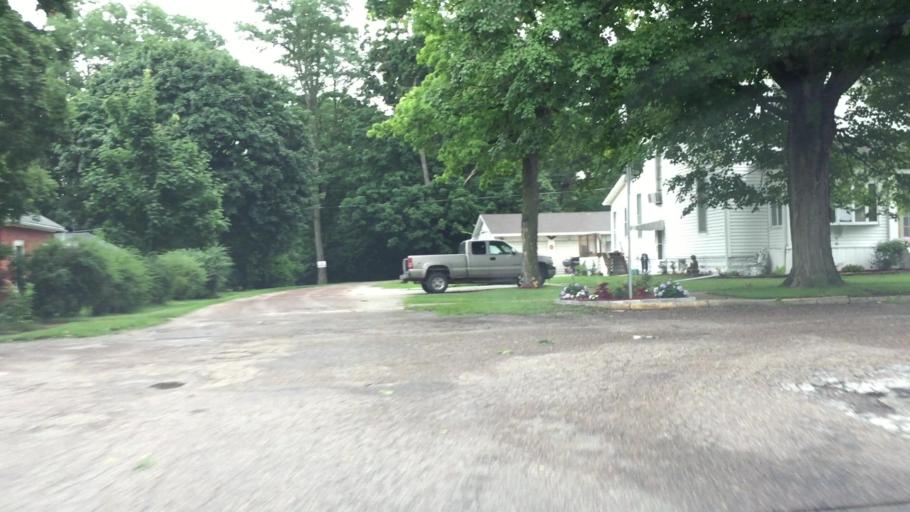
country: US
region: Illinois
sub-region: Hancock County
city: Warsaw
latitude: 40.3622
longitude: -91.4386
